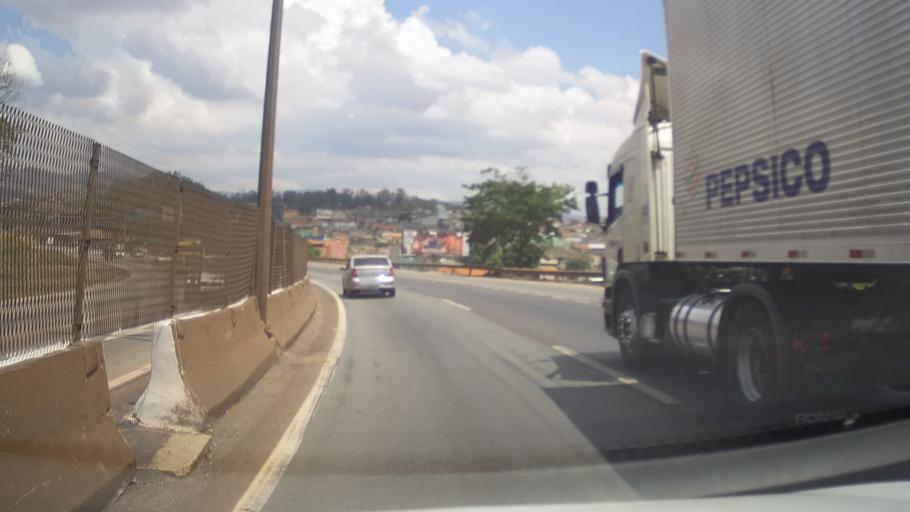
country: BR
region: Minas Gerais
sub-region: Contagem
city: Contagem
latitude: -19.9500
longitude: -44.0087
